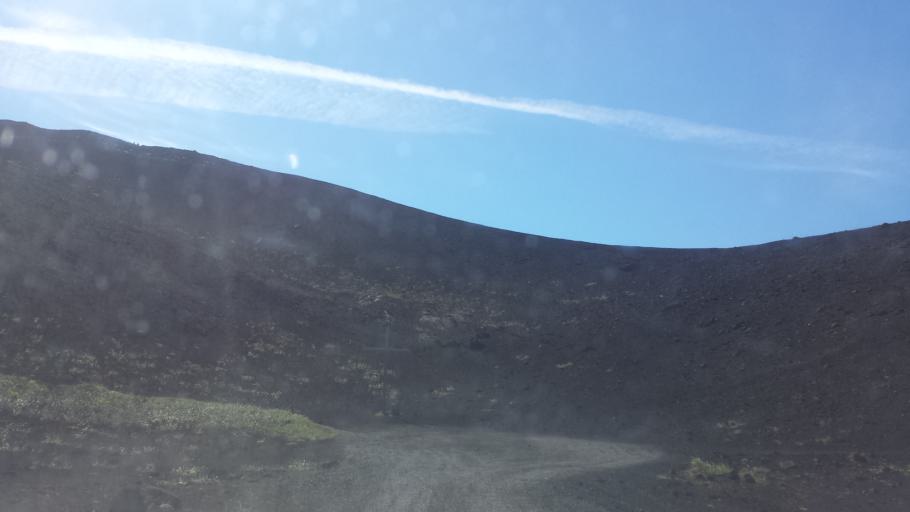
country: IS
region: South
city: Vestmannaeyjar
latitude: 63.4347
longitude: -20.2505
